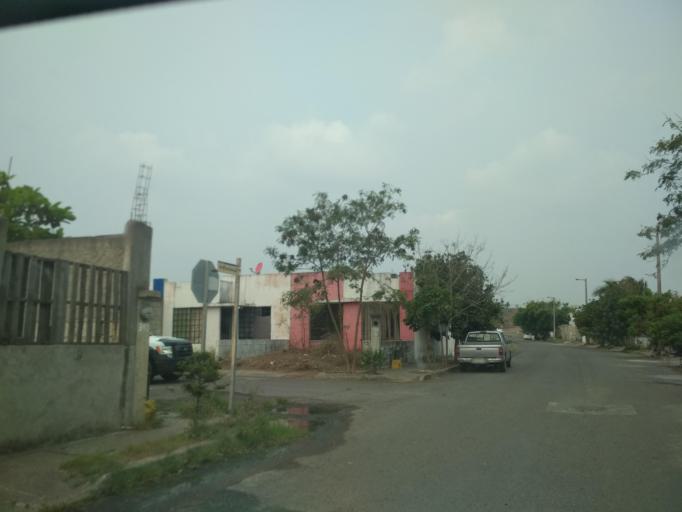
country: MX
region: Veracruz
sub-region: Veracruz
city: Fraccionamiento Geovillas los Pinos
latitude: 19.2321
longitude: -96.2445
